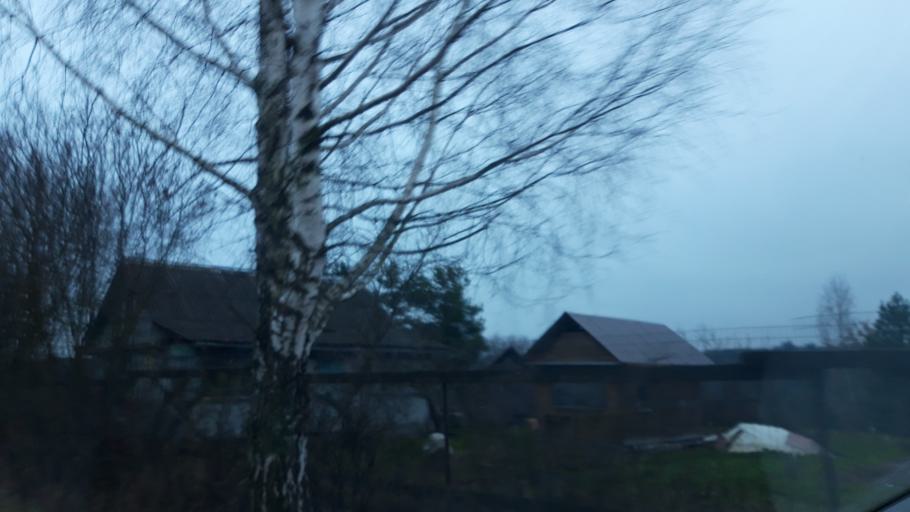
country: RU
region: Moskovskaya
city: Solnechnogorsk
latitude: 56.1224
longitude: 36.9324
